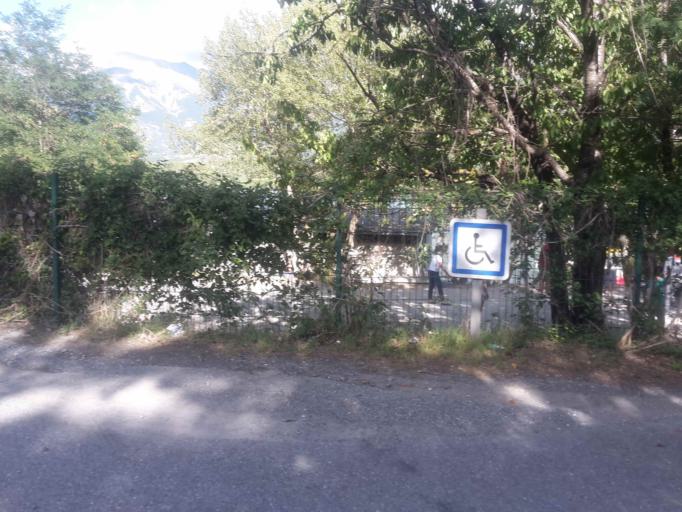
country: FR
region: Provence-Alpes-Cote d'Azur
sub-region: Departement des Hautes-Alpes
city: Embrun
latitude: 44.5487
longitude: 6.4665
